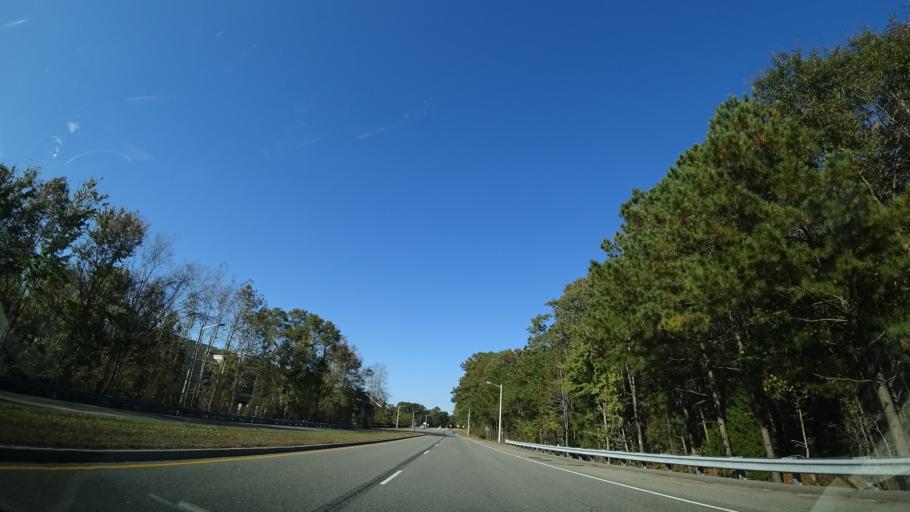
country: US
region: Virginia
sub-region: City of Newport News
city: Newport News
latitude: 36.8913
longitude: -76.4310
